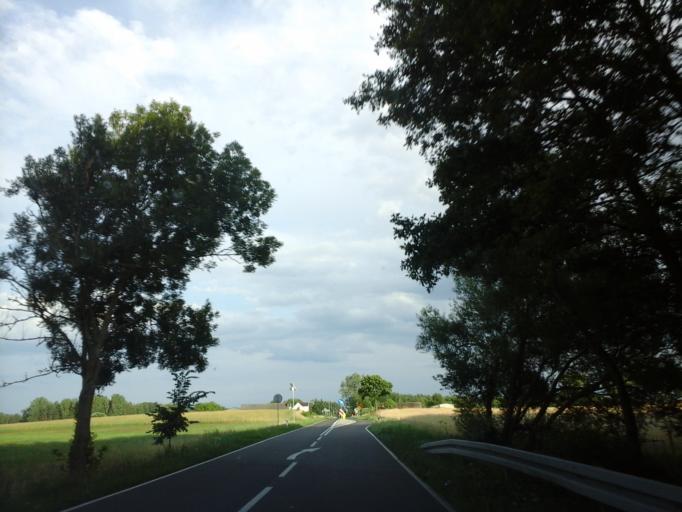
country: PL
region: West Pomeranian Voivodeship
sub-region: Powiat kamienski
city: Golczewo
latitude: 53.8737
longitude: 14.8956
